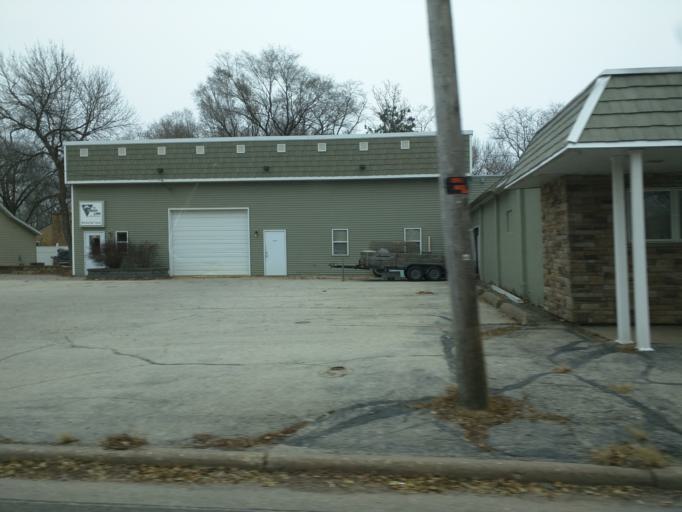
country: US
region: Wisconsin
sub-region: La Crosse County
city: North La Crosse
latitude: 43.8450
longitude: -91.2612
